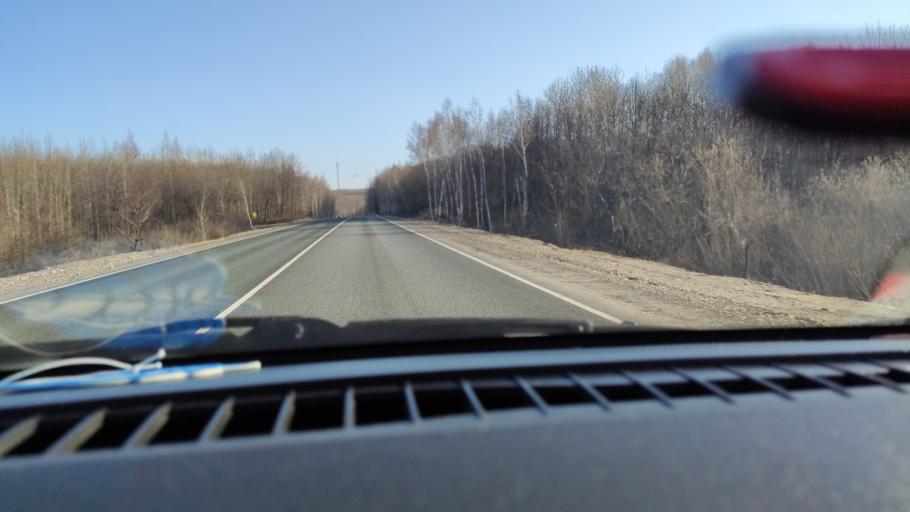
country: RU
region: Saratov
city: Khvalynsk
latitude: 52.4558
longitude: 48.0149
